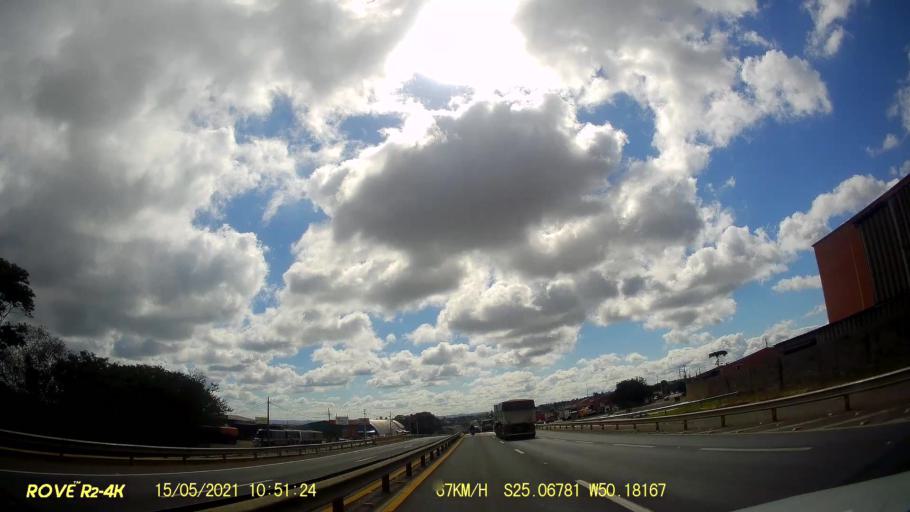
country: BR
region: Parana
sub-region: Ponta Grossa
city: Ponta Grossa
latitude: -25.0680
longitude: -50.1818
